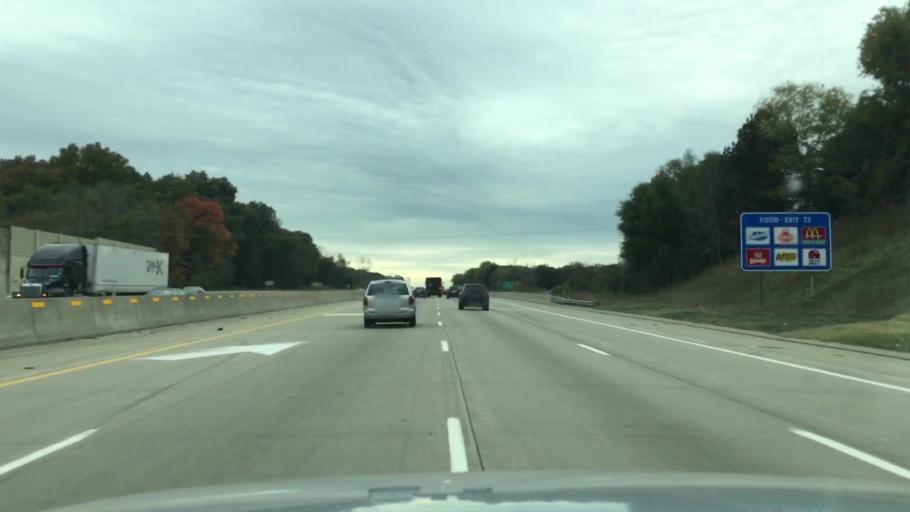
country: US
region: Michigan
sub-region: Kalamazoo County
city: Westwood
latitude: 42.2380
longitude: -85.6471
